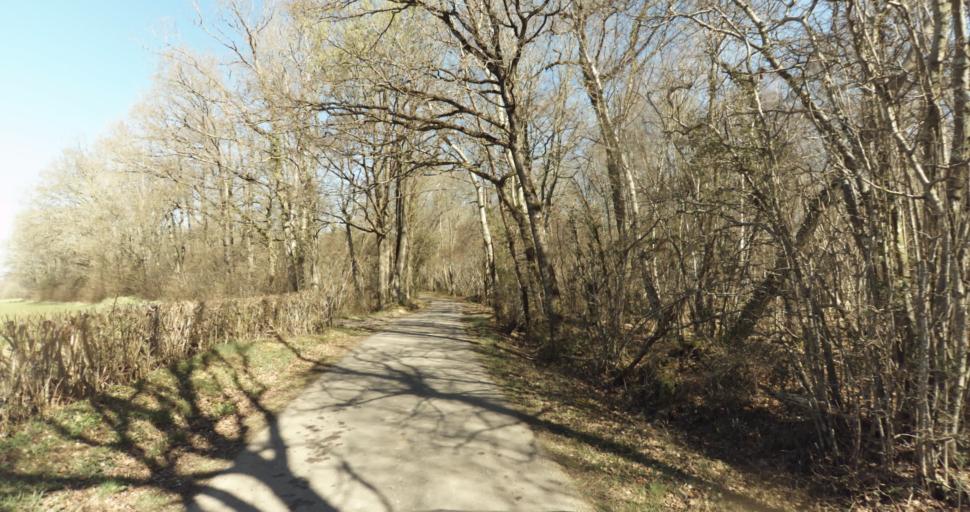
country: FR
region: Lower Normandy
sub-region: Departement du Calvados
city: Livarot
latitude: 48.9878
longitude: 0.0846
